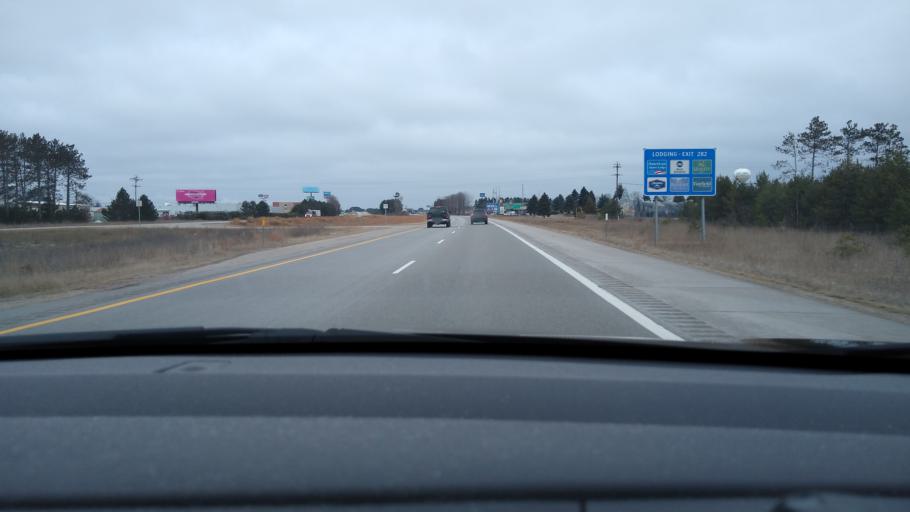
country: US
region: Michigan
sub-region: Otsego County
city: Gaylord
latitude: 45.0163
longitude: -84.6846
